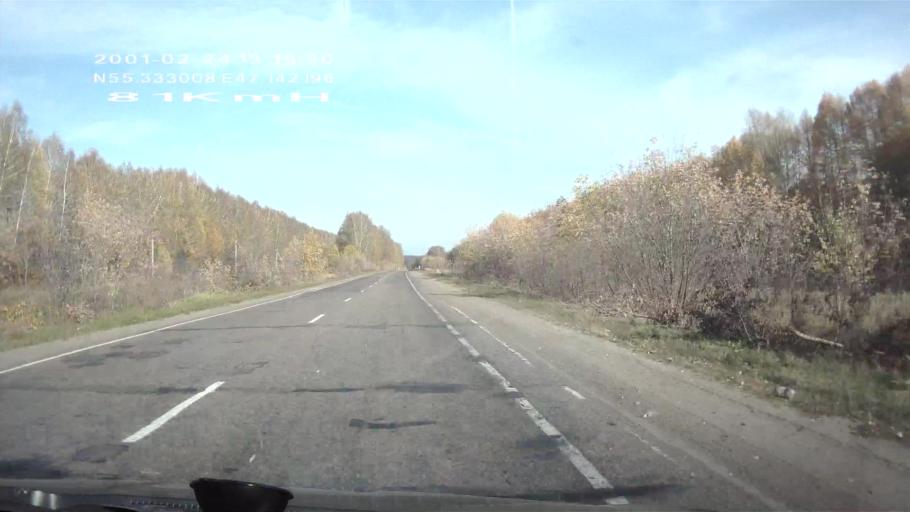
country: RU
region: Chuvashia
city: Ibresi
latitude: 55.3330
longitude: 47.1421
